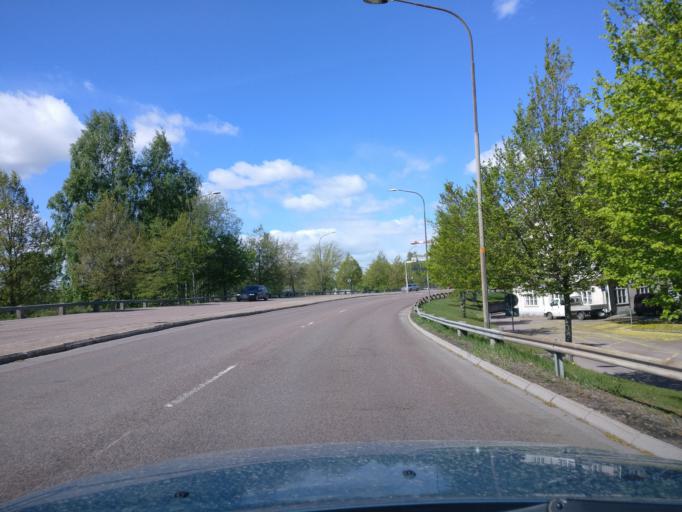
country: SE
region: Vaermland
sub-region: Karlstads Kommun
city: Karlstad
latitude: 59.3789
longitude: 13.4898
